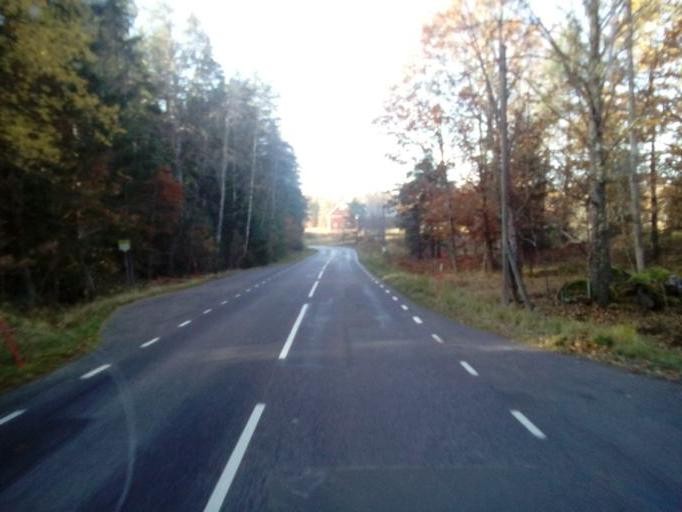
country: SE
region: Kalmar
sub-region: Vimmerby Kommun
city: Vimmerby
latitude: 57.7329
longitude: 16.0804
